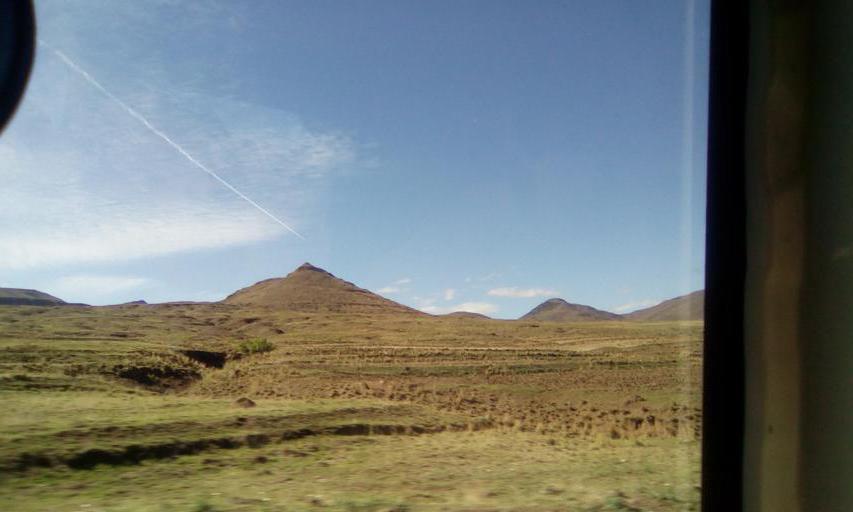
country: LS
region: Qacha's Nek
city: Qacha's Nek
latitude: -30.0390
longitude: 28.2593
